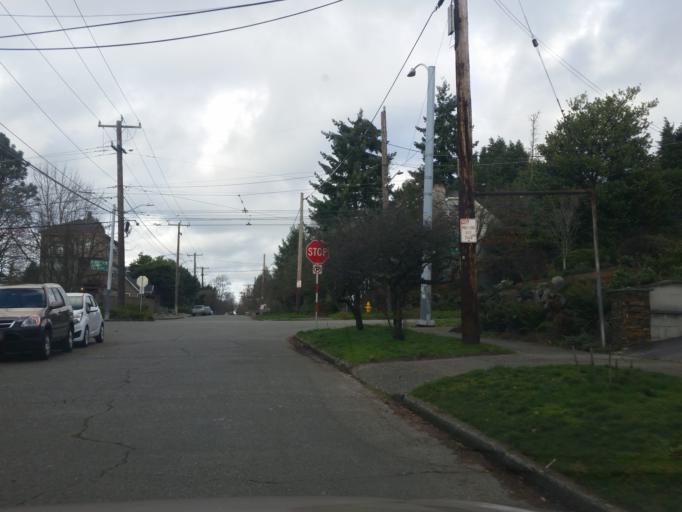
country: US
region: Washington
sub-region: King County
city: Seattle
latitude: 47.6618
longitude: -122.3554
